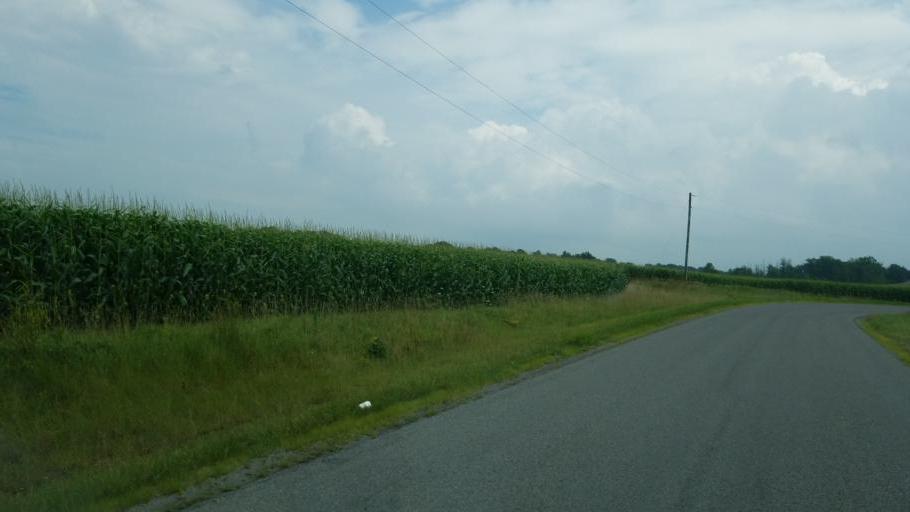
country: US
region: Ohio
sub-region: Logan County
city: Northwood
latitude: 40.4187
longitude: -83.7245
